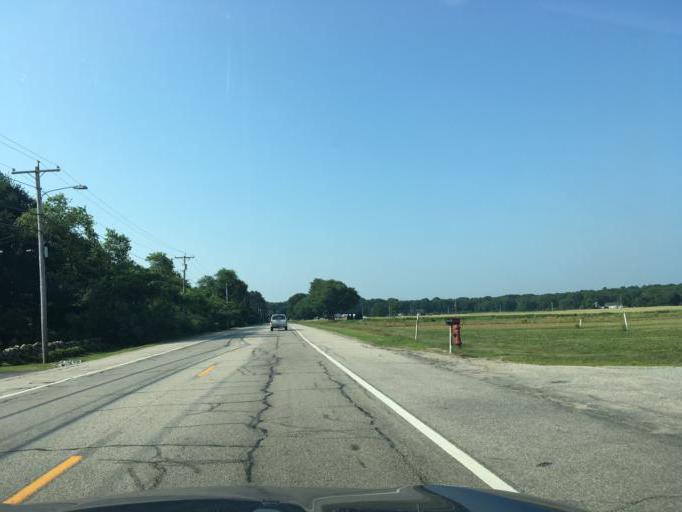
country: US
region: Rhode Island
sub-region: Washington County
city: Exeter
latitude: 41.5647
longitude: -71.5176
